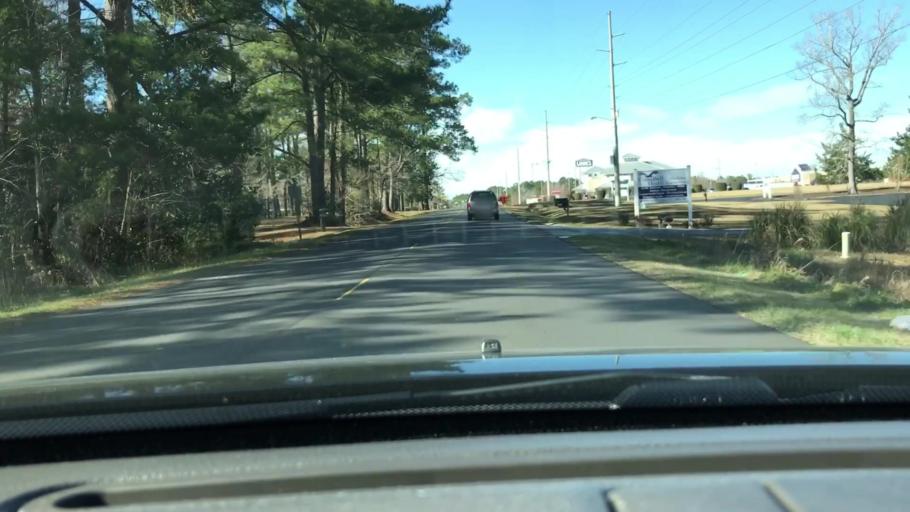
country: US
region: North Carolina
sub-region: Brunswick County
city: Shallotte
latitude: 33.9714
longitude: -78.3970
